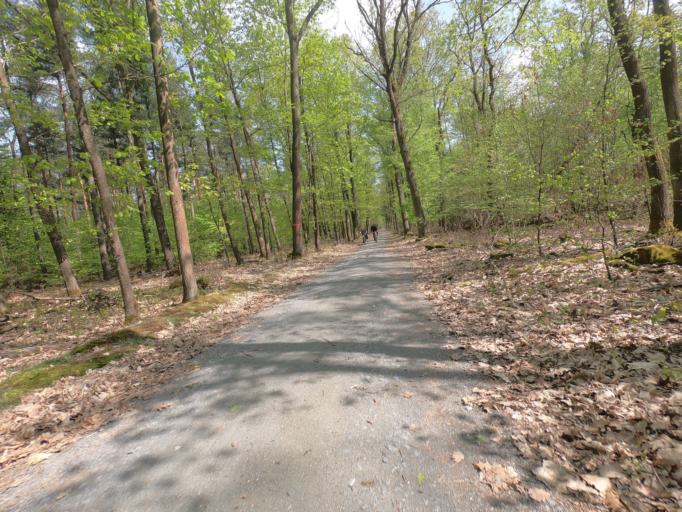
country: DE
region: Hesse
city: Niederrad
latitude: 50.0446
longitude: 8.6202
